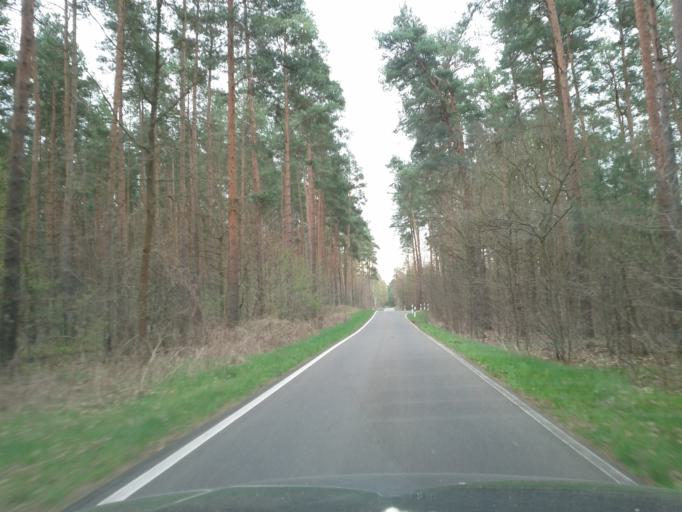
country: DE
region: Brandenburg
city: Spreenhagen
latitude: 52.3859
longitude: 13.8521
